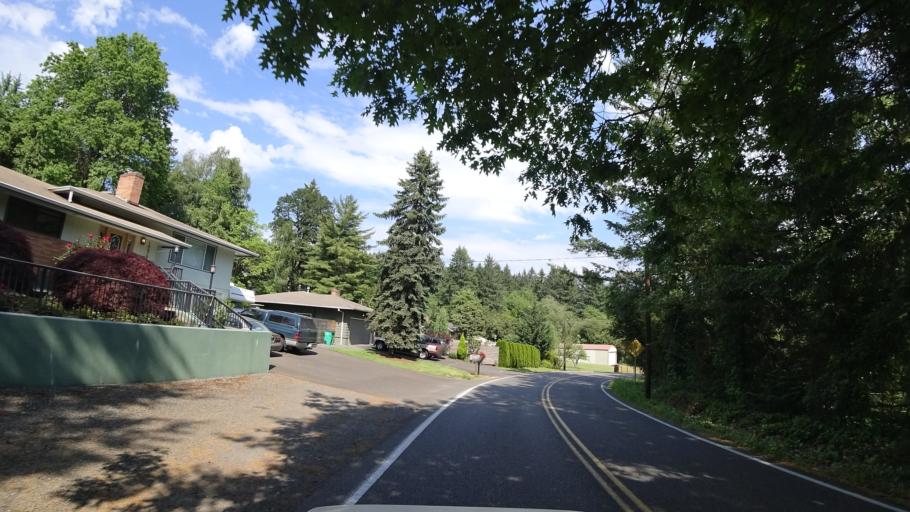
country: US
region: Oregon
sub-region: Washington County
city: Metzger
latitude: 45.4499
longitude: -122.7391
